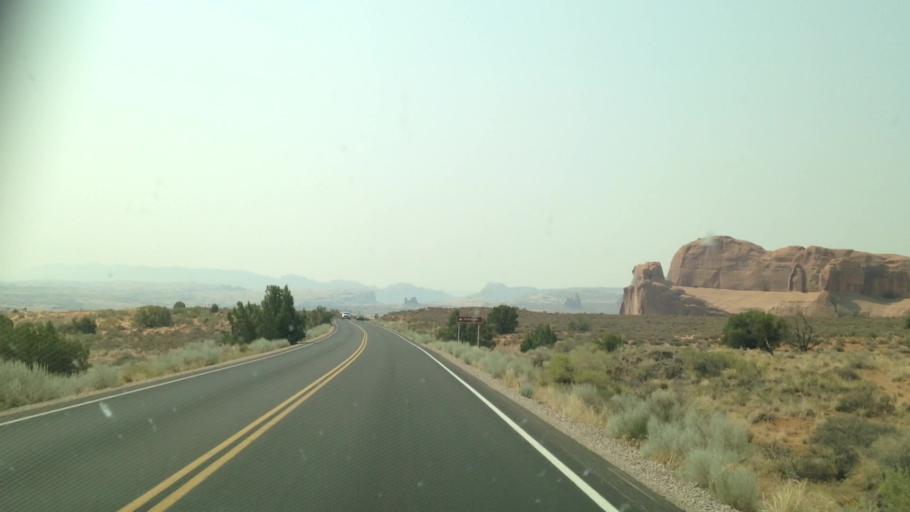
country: US
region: Utah
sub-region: Grand County
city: Moab
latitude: 38.6676
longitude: -109.5880
